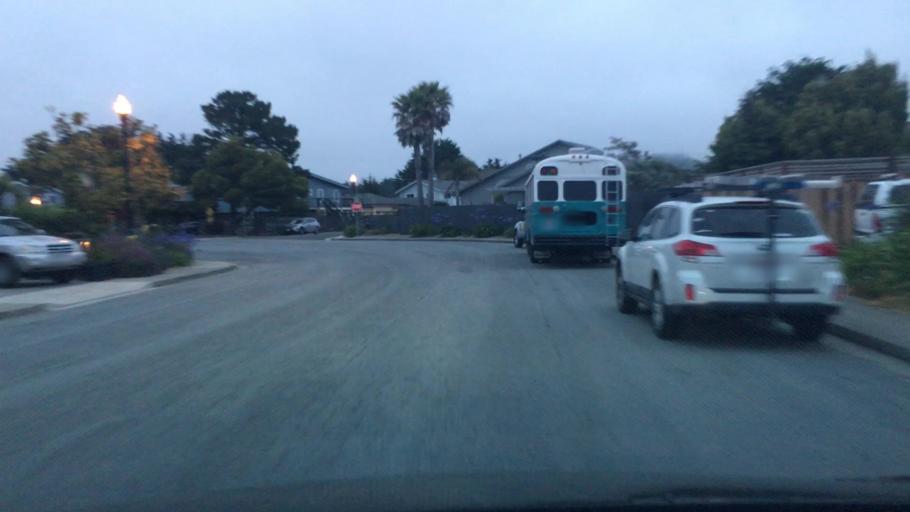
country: US
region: California
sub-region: San Mateo County
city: Half Moon Bay
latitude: 37.4598
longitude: -122.4393
